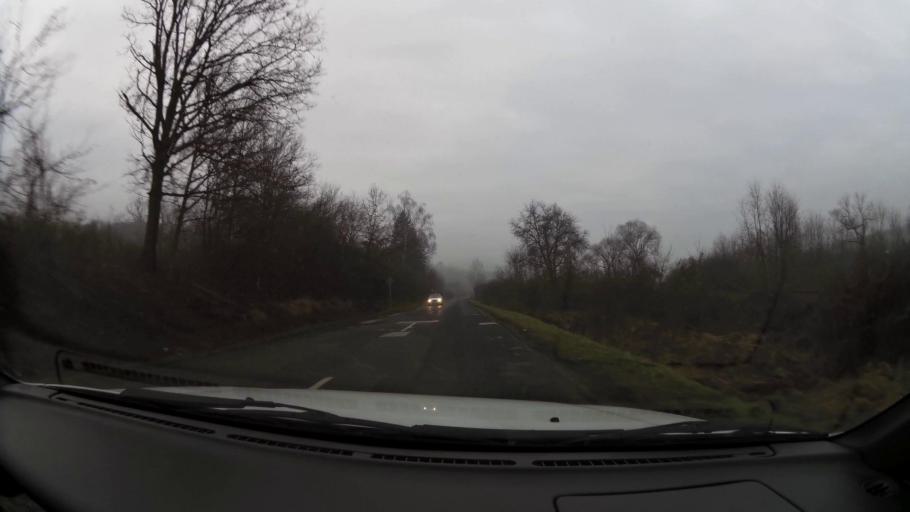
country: HU
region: Borsod-Abauj-Zemplen
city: Rudabanya
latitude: 48.3507
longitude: 20.6391
